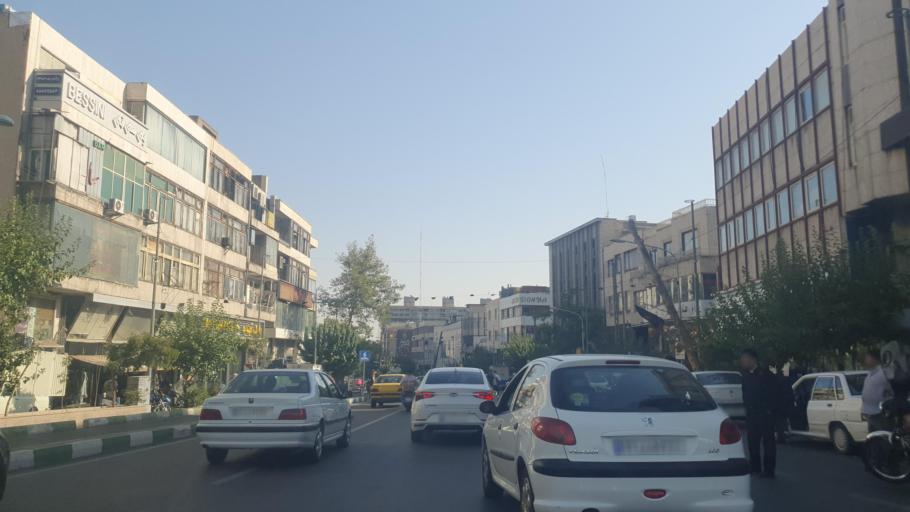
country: IR
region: Tehran
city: Tehran
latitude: 35.7151
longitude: 51.4261
